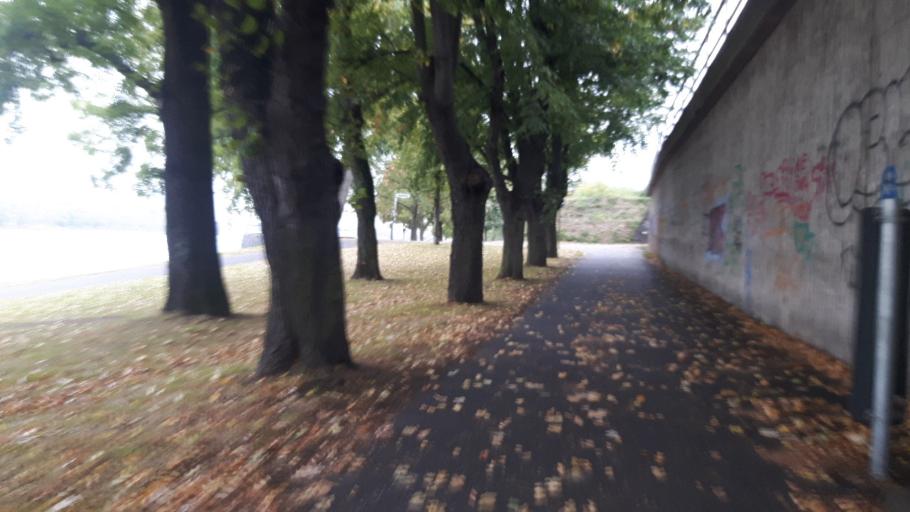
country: DE
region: North Rhine-Westphalia
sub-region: Regierungsbezirk Koln
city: Konigswinter
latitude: 50.7121
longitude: 7.1625
